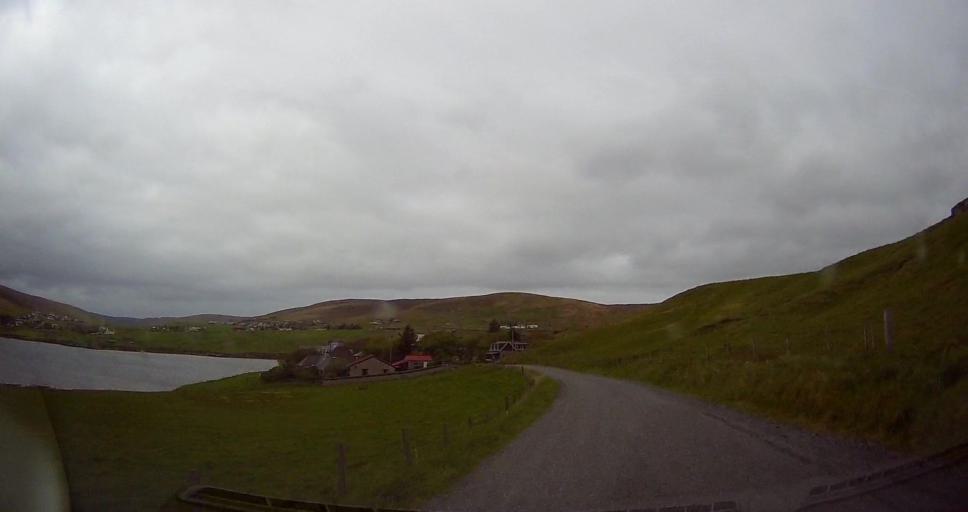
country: GB
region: Scotland
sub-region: Shetland Islands
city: Lerwick
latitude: 60.3474
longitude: -1.2698
